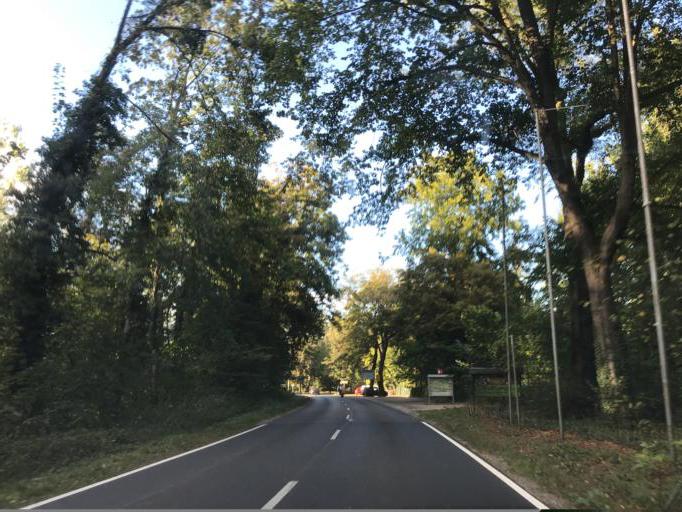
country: DE
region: Brandenburg
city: Eberswalde
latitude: 52.8264
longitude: 13.8307
